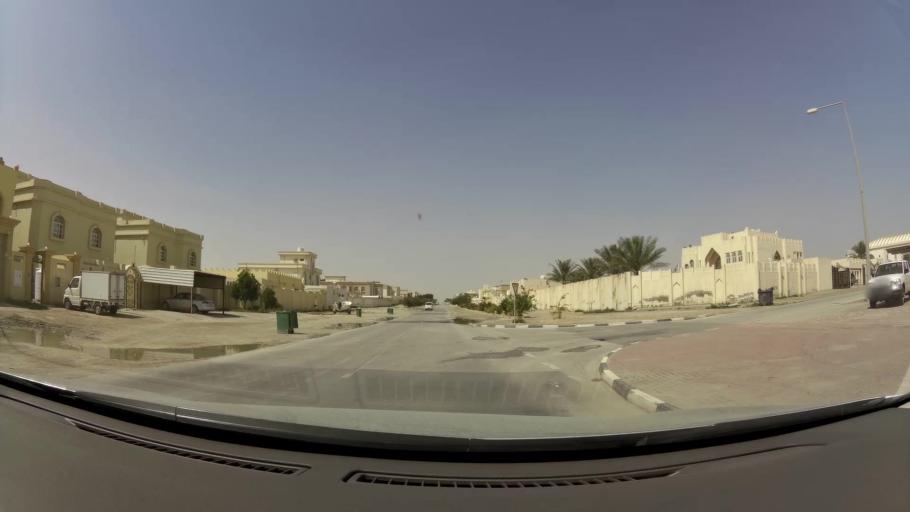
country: QA
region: Baladiyat Umm Salal
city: Umm Salal Muhammad
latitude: 25.3771
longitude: 51.4202
